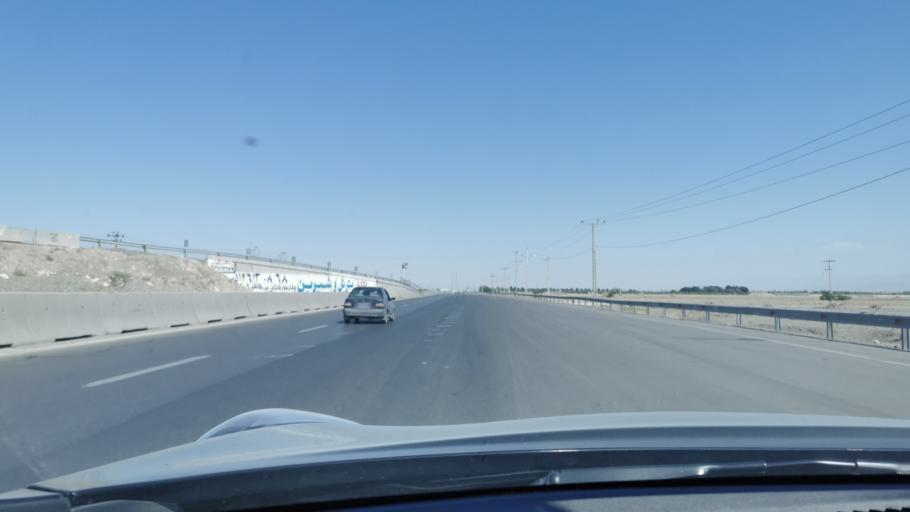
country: IR
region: Razavi Khorasan
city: Chenaran
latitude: 36.6186
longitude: 59.1588
